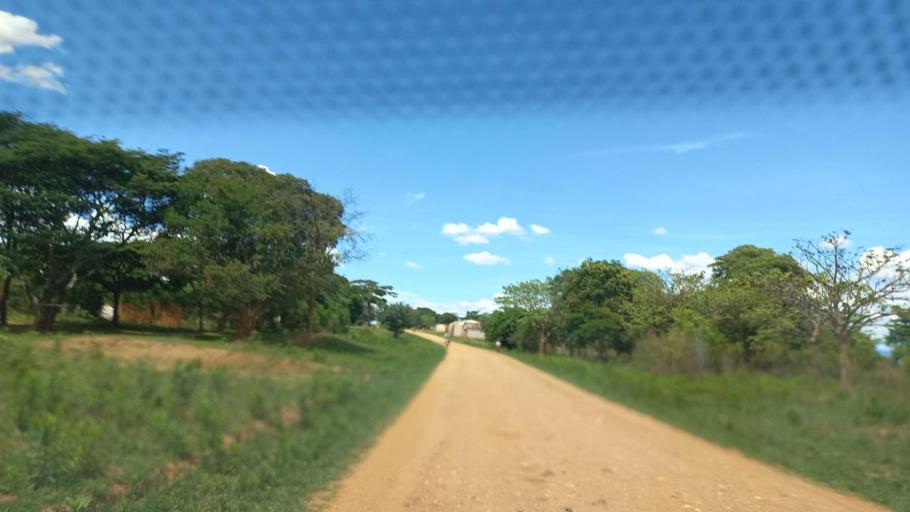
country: ZM
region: North-Western
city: Mwinilunga
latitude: -12.3069
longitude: 24.2616
